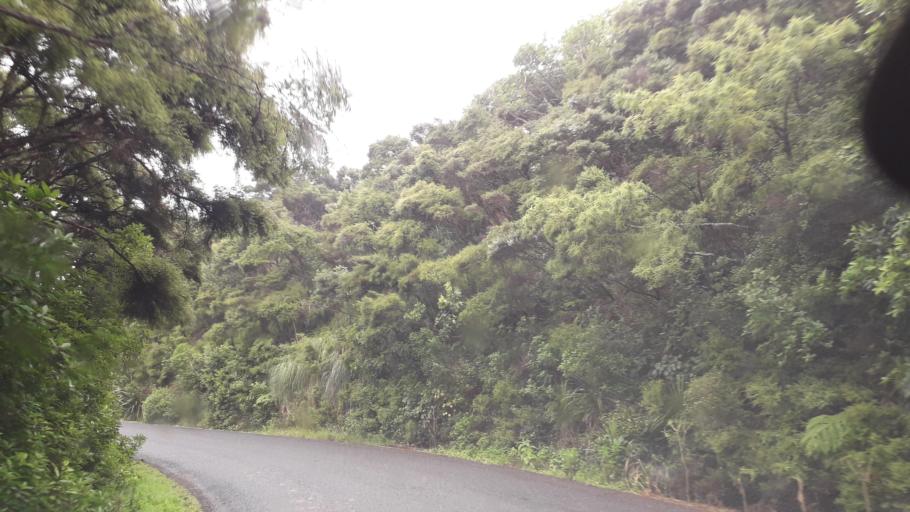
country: NZ
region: Northland
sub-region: Far North District
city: Paihia
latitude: -35.2225
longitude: 174.2596
